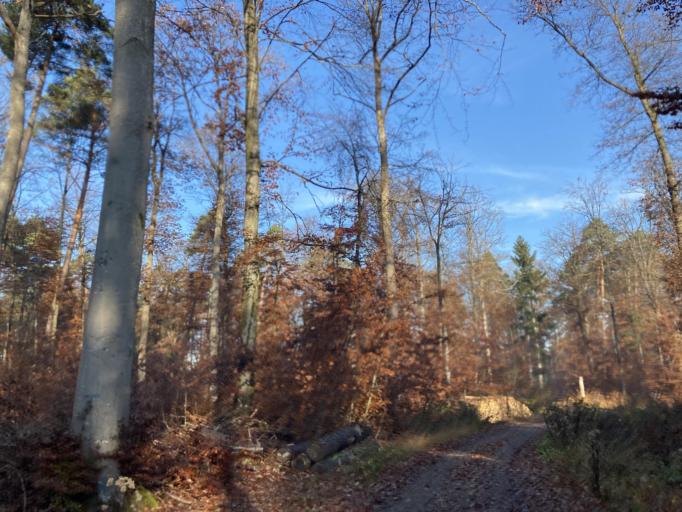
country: DE
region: Baden-Wuerttemberg
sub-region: Regierungsbezirk Stuttgart
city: Hildrizhausen
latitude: 48.5824
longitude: 8.9674
